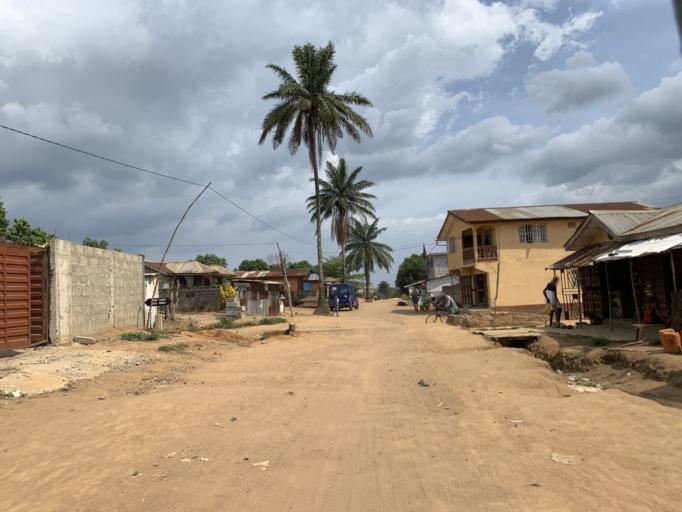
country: SL
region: Western Area
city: Waterloo
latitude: 8.3388
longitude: -13.0528
